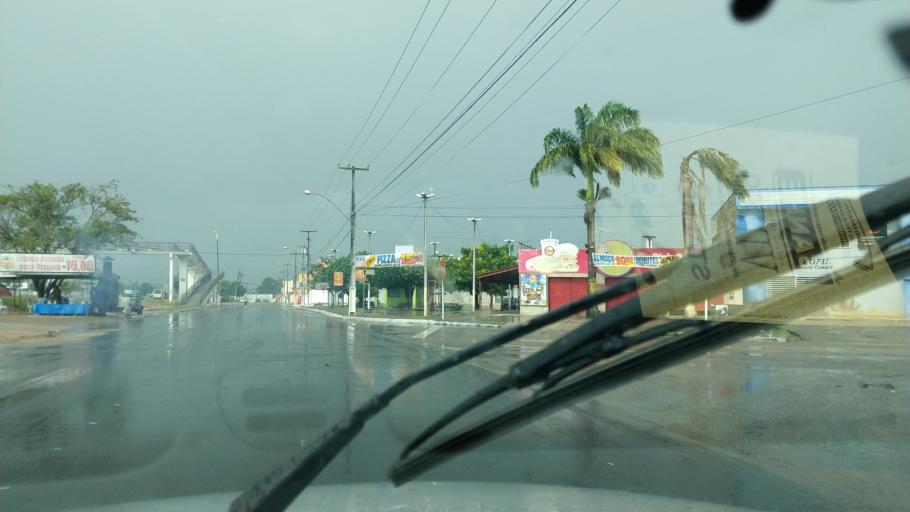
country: BR
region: Rio Grande do Norte
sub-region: Parnamirim
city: Parnamirim
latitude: -5.9263
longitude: -35.2652
